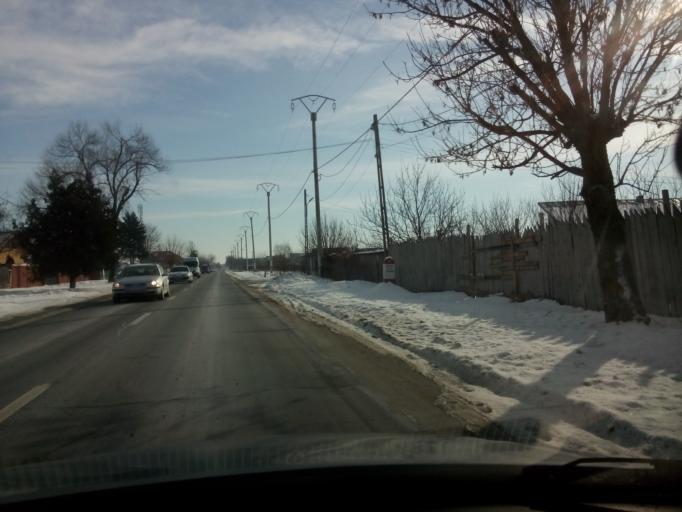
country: RO
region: Calarasi
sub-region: Comuna Frumusani
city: Frumusani
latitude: 44.3076
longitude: 26.2948
